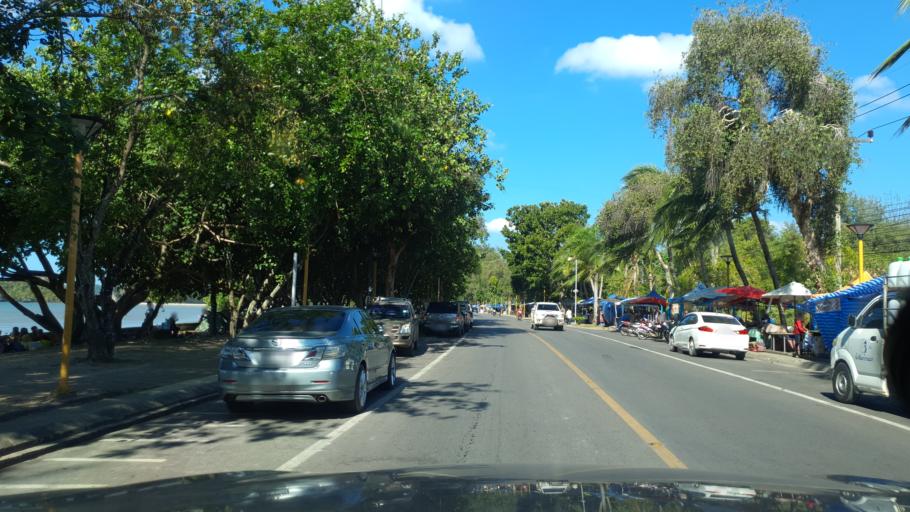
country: TH
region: Phangnga
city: Ban Ao Nang
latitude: 8.0441
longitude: 98.8076
